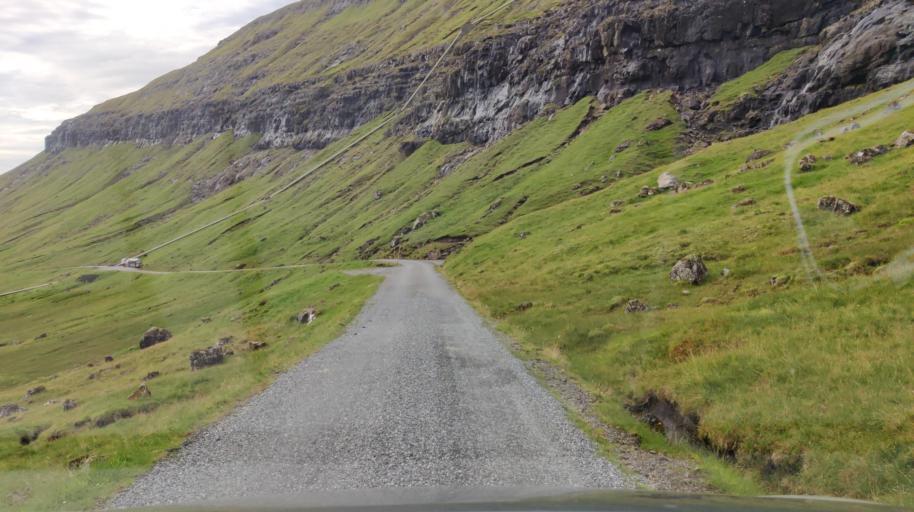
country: FO
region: Streymoy
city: Vestmanna
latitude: 62.1551
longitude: -7.1022
